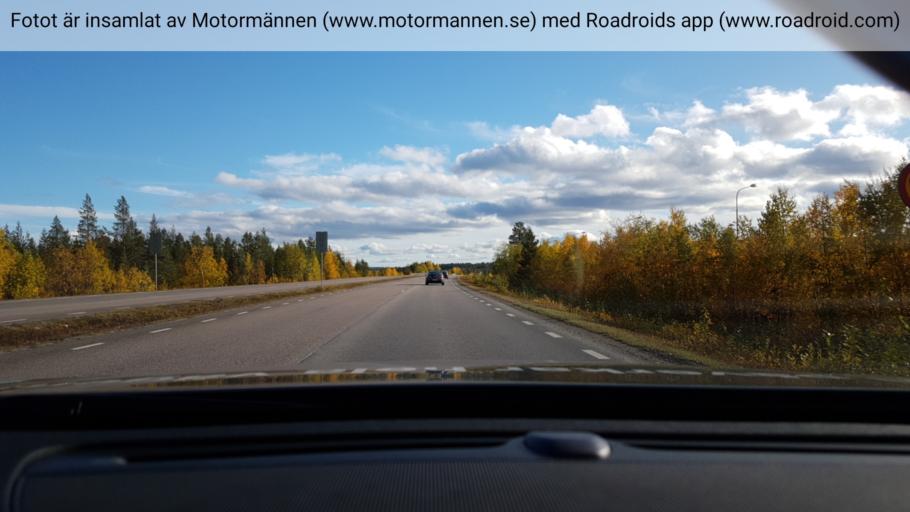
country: SE
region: Norrbotten
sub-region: Gallivare Kommun
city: Malmberget
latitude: 67.1592
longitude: 20.6580
